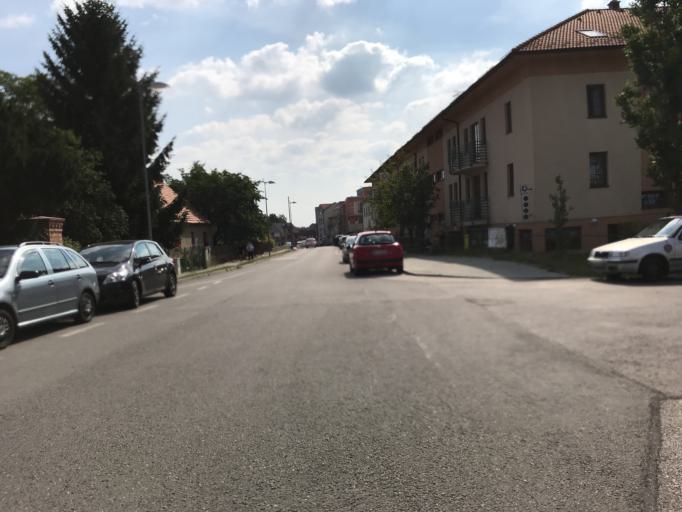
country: CZ
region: Jihocesky
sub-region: Okres Jindrichuv Hradec
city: Trebon
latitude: 49.0043
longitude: 14.7559
